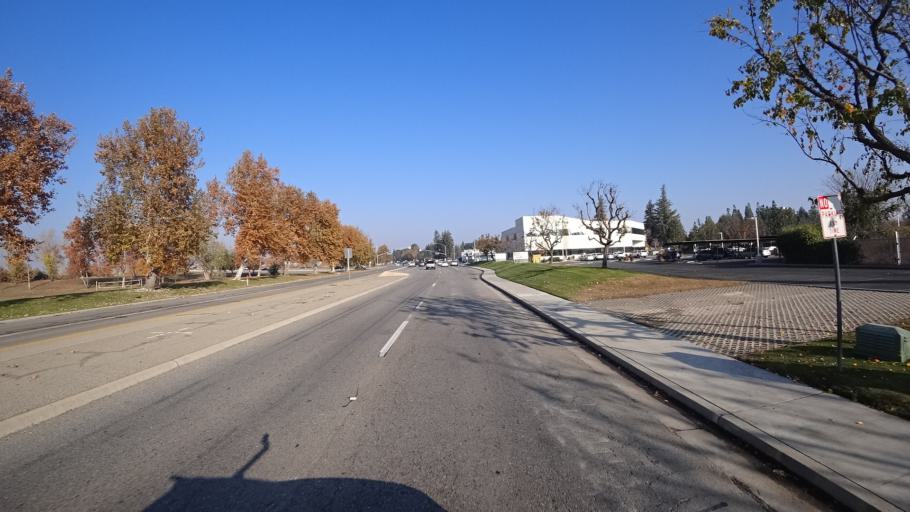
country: US
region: California
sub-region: Kern County
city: Greenacres
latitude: 35.3644
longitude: -119.0670
